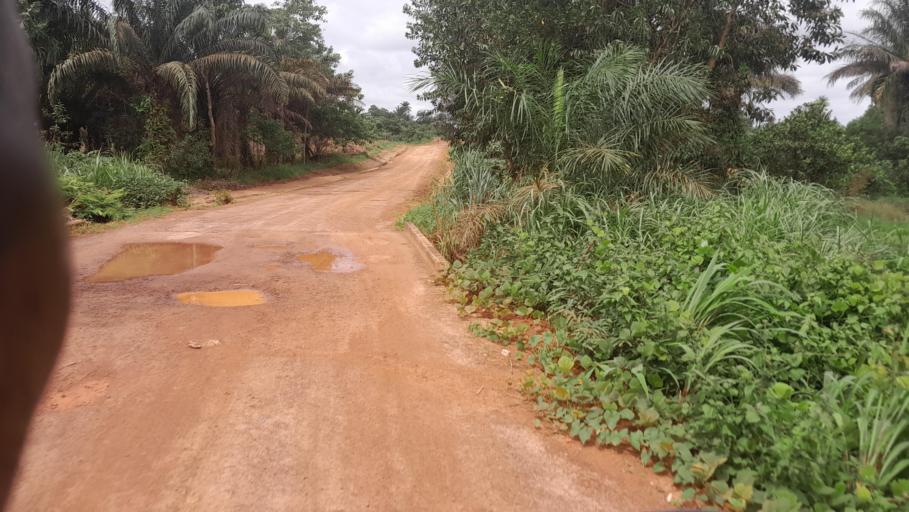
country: GN
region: Boke
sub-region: Boffa
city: Boffa
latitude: 10.0983
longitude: -13.8551
